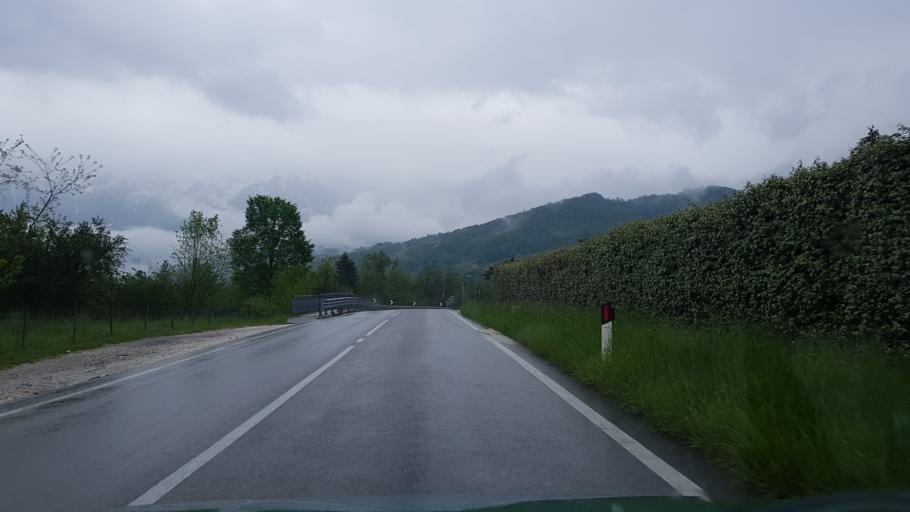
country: IT
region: Veneto
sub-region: Provincia di Belluno
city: Puos d'Alpago
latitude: 46.1376
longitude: 12.3703
